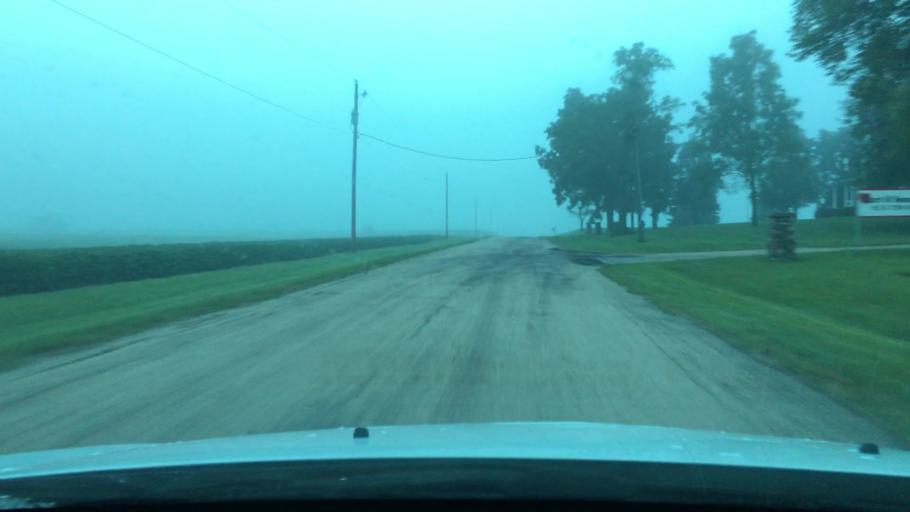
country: US
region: Illinois
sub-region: Ogle County
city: Rochelle
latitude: 41.9157
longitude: -88.9806
